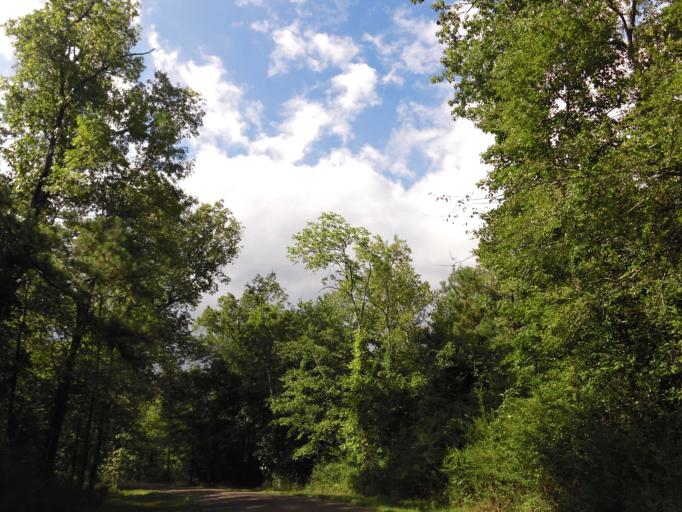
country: US
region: Georgia
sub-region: Walker County
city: Chickamauga
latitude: 34.9024
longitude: -85.2677
